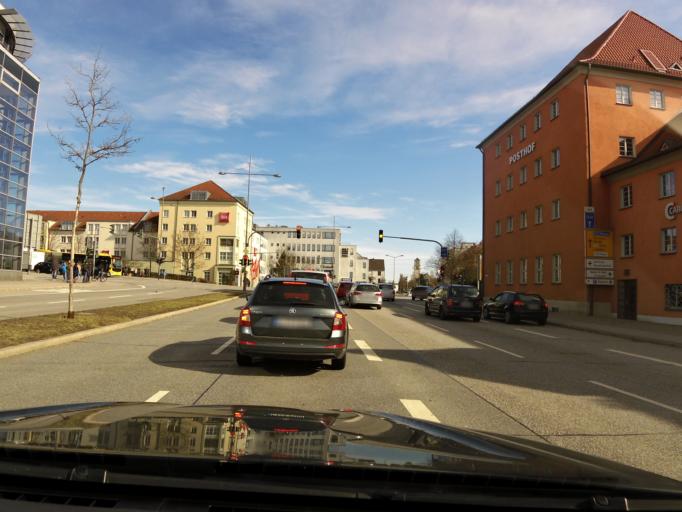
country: DE
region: Bavaria
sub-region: Upper Palatinate
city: Regensburg
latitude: 49.0102
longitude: 12.1010
